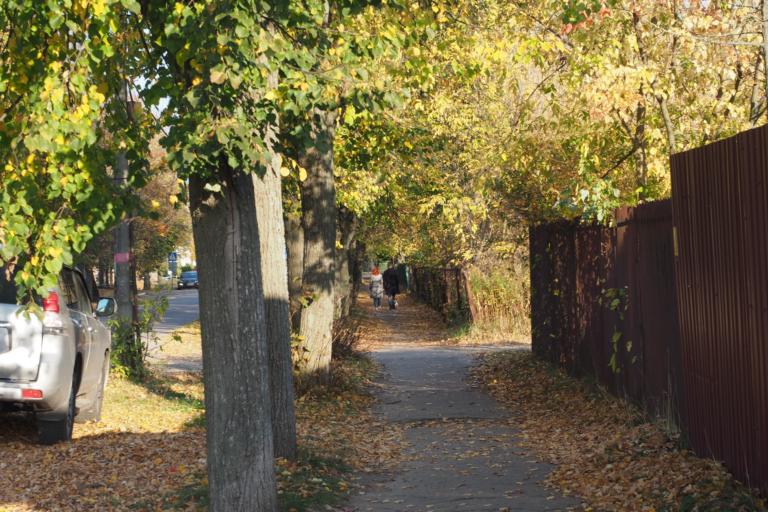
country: RU
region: Moskovskaya
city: Kurovskoye
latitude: 55.5764
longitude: 38.9141
